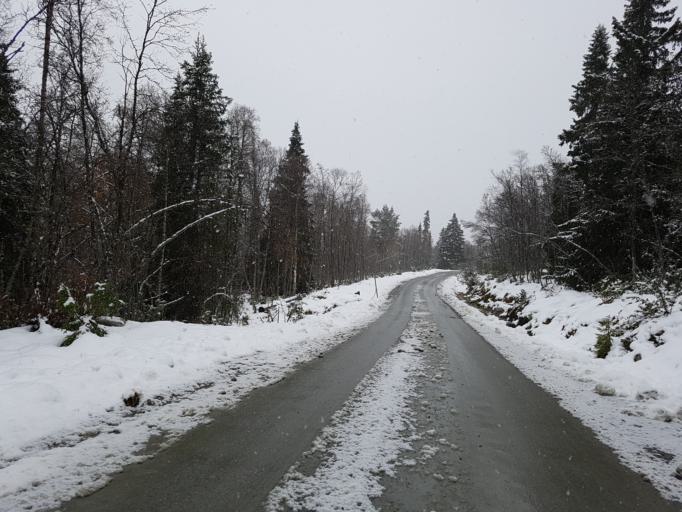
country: NO
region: Oppland
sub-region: Sel
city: Otta
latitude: 61.7922
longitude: 9.7181
